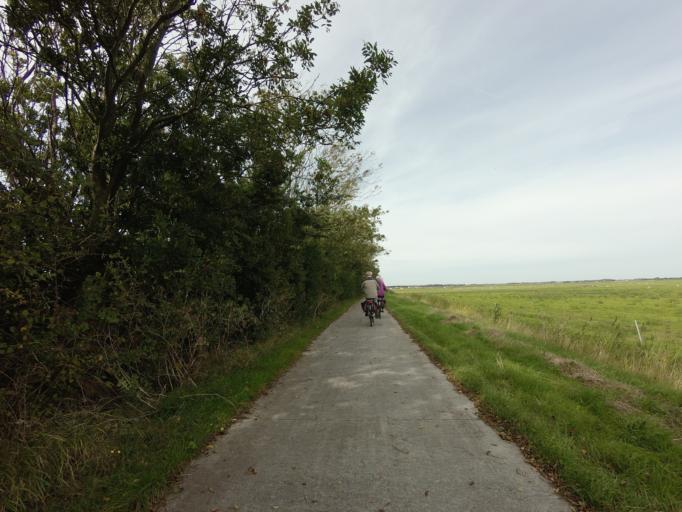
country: NL
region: North Holland
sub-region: Gemeente Texel
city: Den Burg
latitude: 53.0737
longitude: 4.8079
